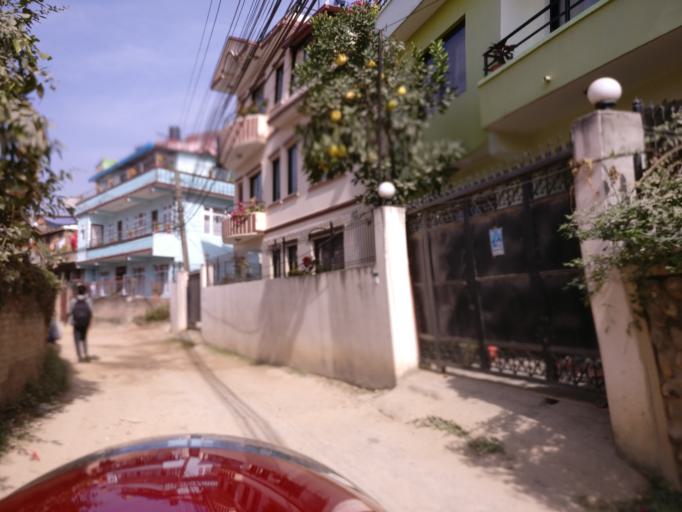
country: NP
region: Central Region
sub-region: Bagmati Zone
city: Patan
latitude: 27.6627
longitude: 85.3106
